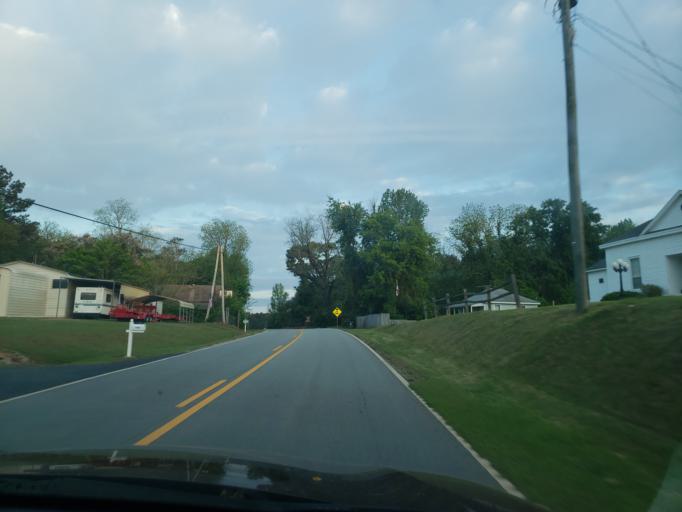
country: US
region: Alabama
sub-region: Tallapoosa County
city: Dadeville
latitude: 32.7012
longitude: -85.7439
